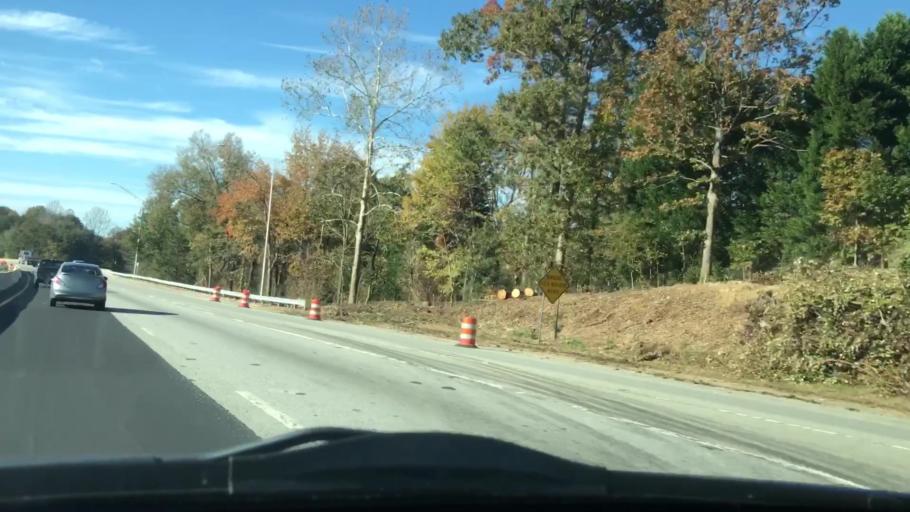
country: US
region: North Carolina
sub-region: Guilford County
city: High Point
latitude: 36.0035
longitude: -79.9947
